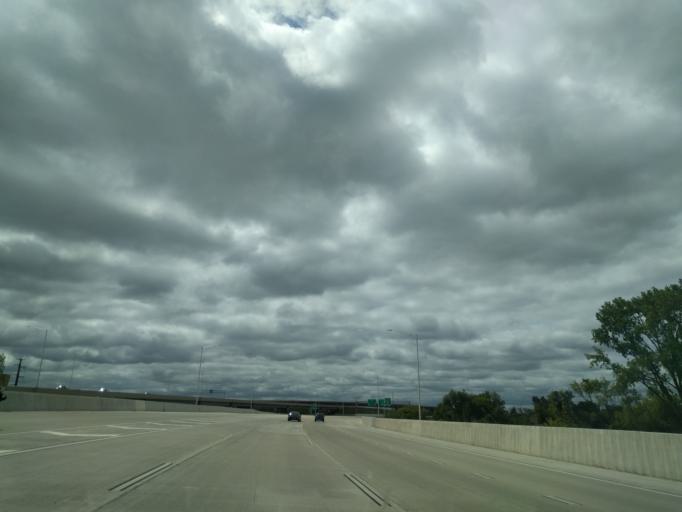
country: US
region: Wisconsin
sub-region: Brown County
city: Howard
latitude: 44.5661
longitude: -88.0490
